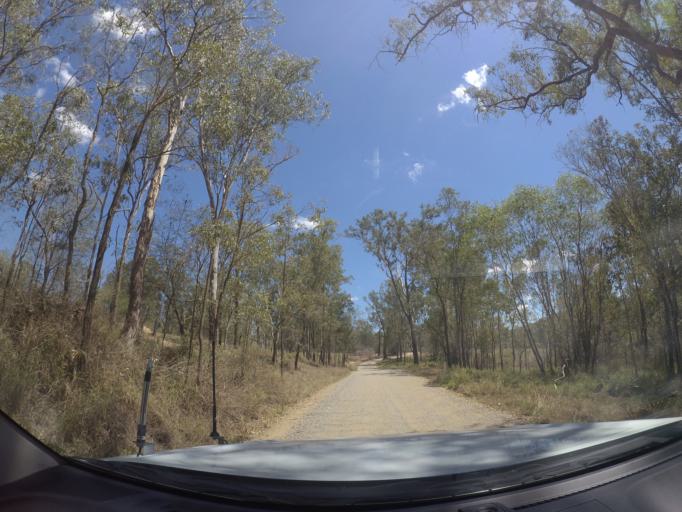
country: AU
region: Queensland
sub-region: Logan
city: North Maclean
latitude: -27.8333
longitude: 152.8682
